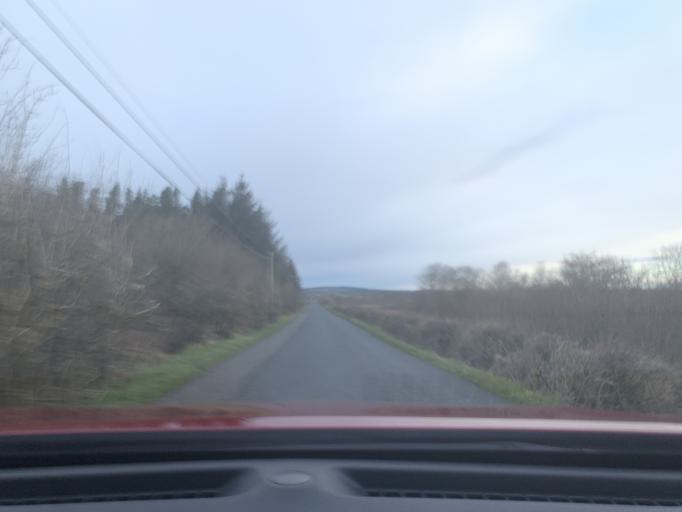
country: IE
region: Connaught
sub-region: Roscommon
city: Ballaghaderreen
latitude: 53.8826
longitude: -8.5658
